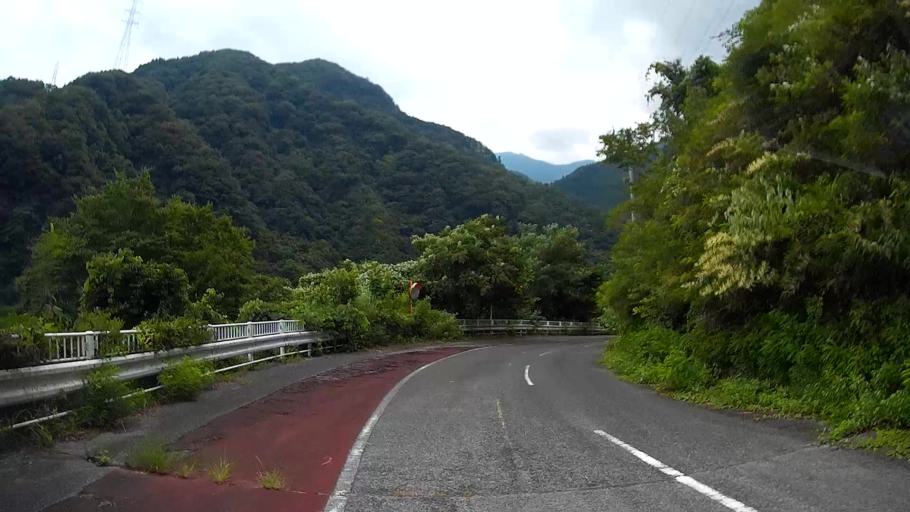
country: JP
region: Saitama
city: Chichibu
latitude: 35.9325
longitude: 139.0583
